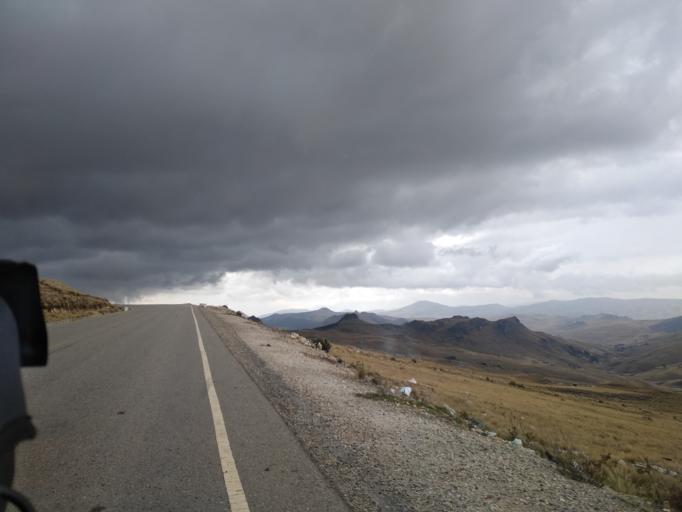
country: PE
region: La Libertad
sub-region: Provincia de Santiago de Chuco
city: Quiruvilca
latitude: -7.9924
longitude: -78.3014
